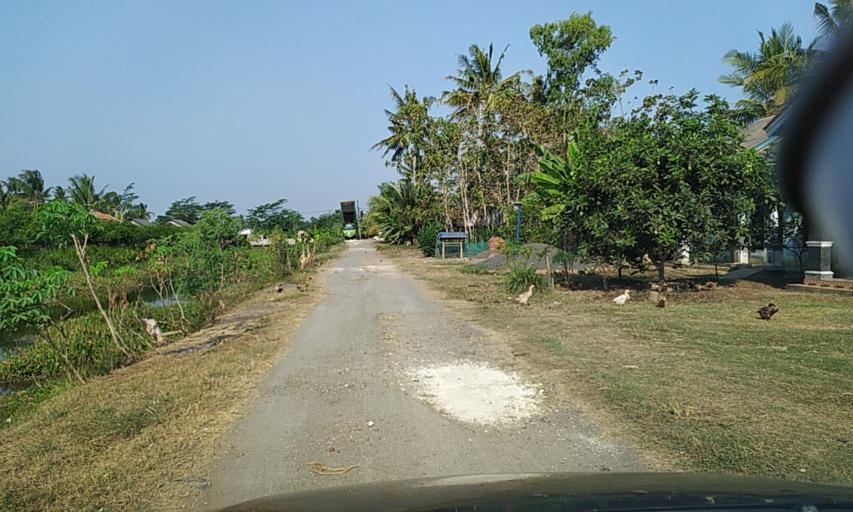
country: ID
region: Central Java
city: Cipari
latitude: -7.5481
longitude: 108.8136
